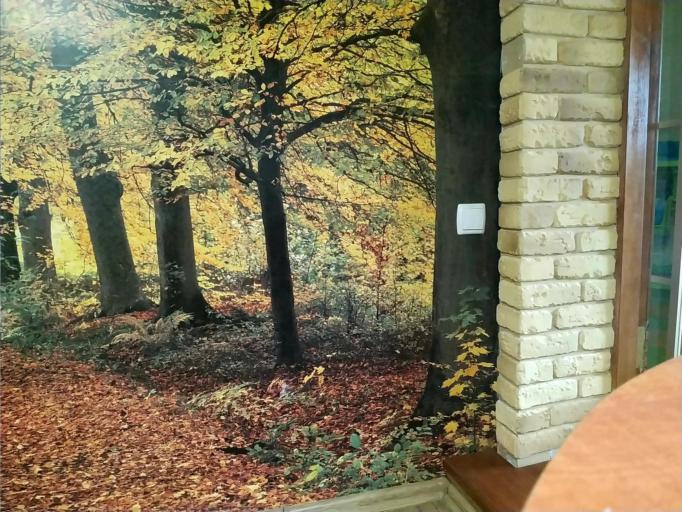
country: RU
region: Smolensk
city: Verkhnedneprovskiy
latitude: 54.9917
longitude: 33.2737
